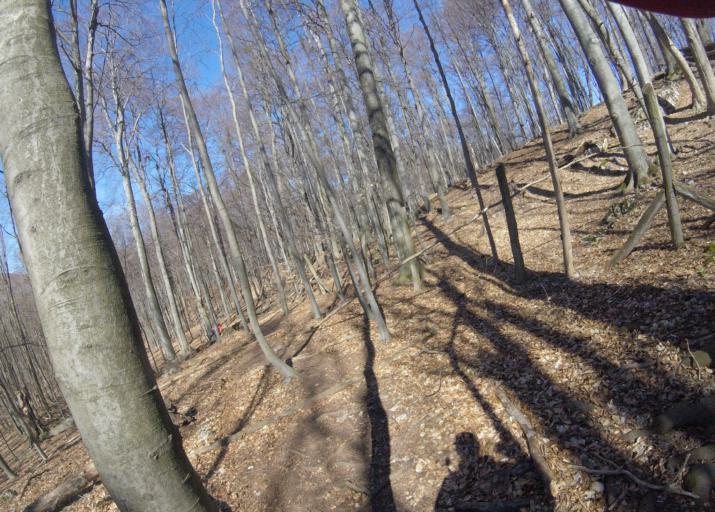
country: HU
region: Heves
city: Szilvasvarad
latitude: 48.0582
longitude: 20.4442
